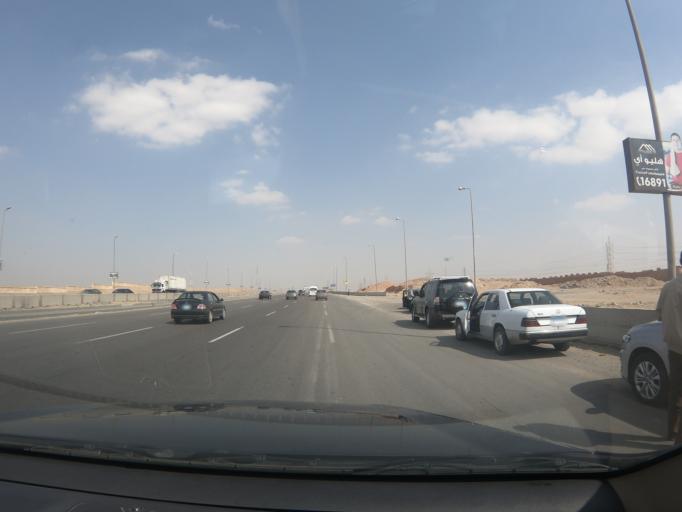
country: EG
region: Muhafazat al Qalyubiyah
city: Al Khankah
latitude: 30.0861
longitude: 31.5252
